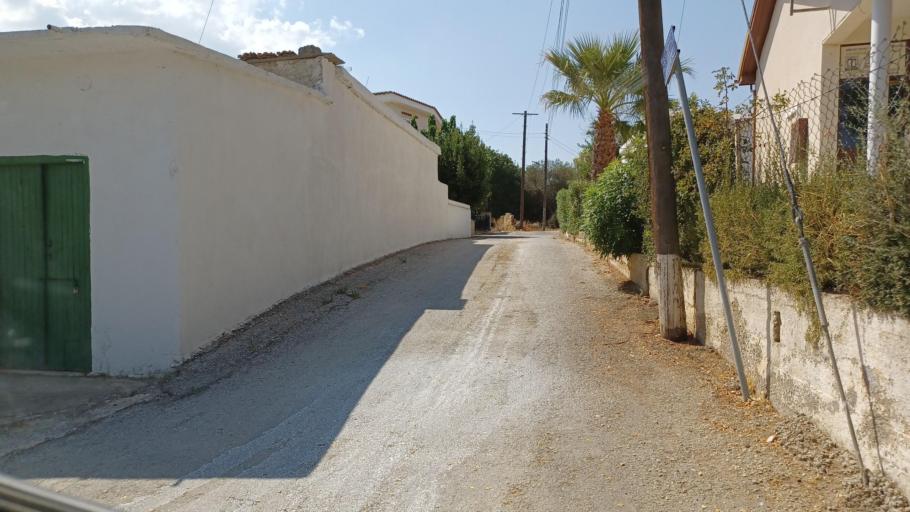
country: CY
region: Pafos
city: Tala
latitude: 34.9240
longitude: 32.4750
